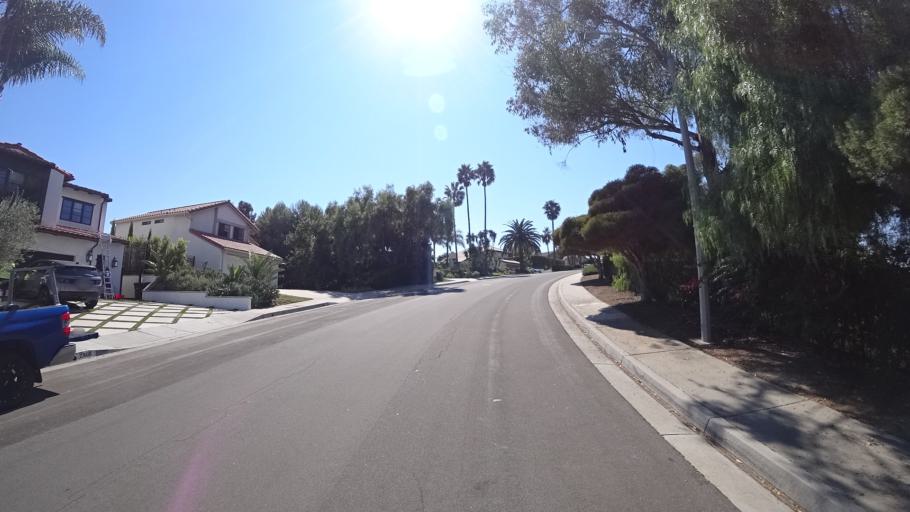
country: US
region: California
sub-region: Orange County
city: San Clemente
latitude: 33.4606
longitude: -117.6244
